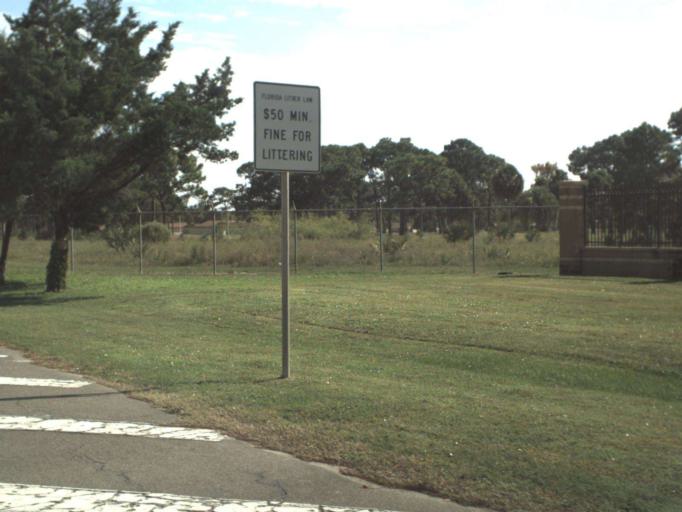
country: US
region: Florida
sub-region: Bay County
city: Tyndall Air Force Base
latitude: 30.0698
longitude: -85.5901
